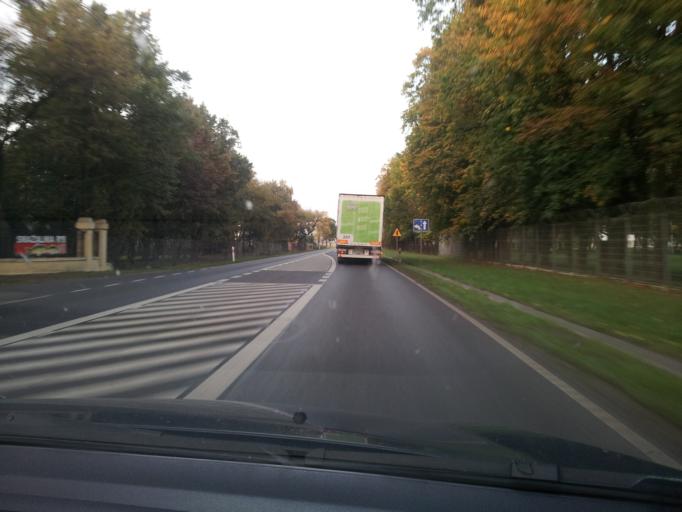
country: PL
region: Kujawsko-Pomorskie
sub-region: Powiat inowroclawski
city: Inowroclaw
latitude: 52.8269
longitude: 18.3067
